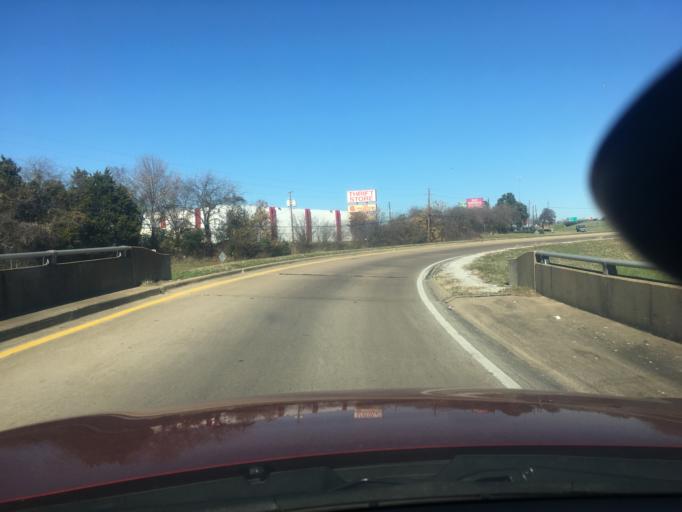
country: US
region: Texas
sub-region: Dallas County
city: Cockrell Hill
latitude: 32.6880
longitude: -96.8243
